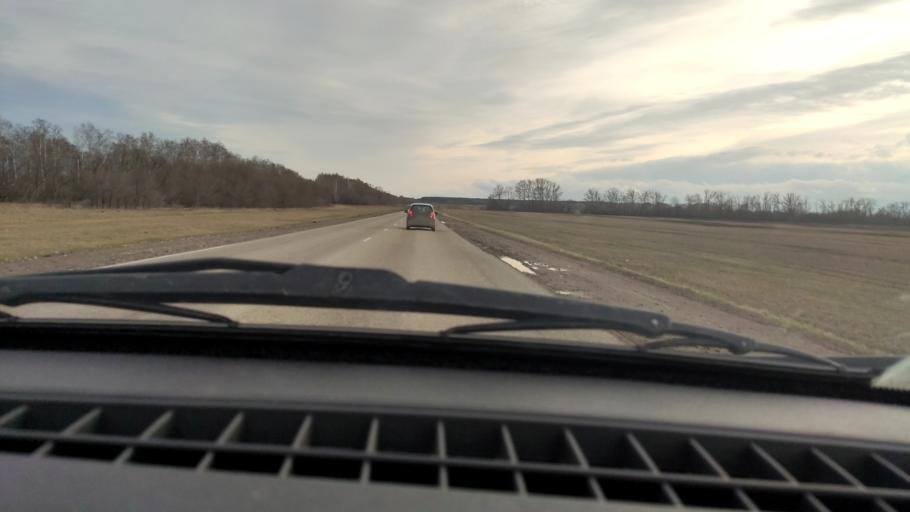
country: RU
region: Bashkortostan
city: Davlekanovo
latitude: 54.2634
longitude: 55.0927
